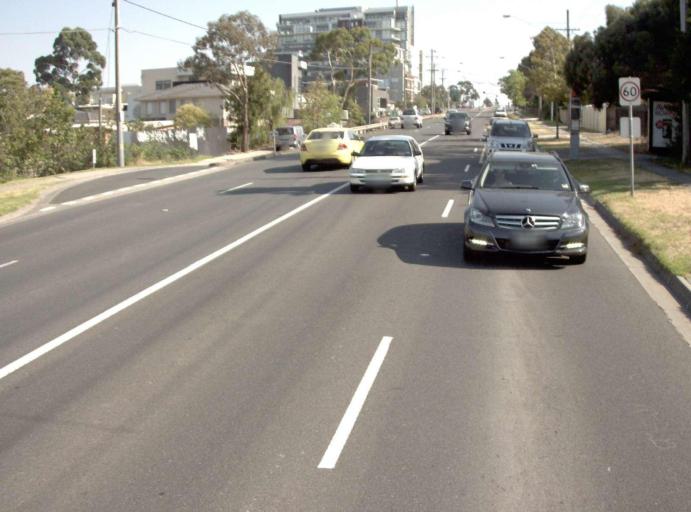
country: AU
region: Victoria
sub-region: Manningham
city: Doncaster
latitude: -37.7914
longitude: 145.1256
